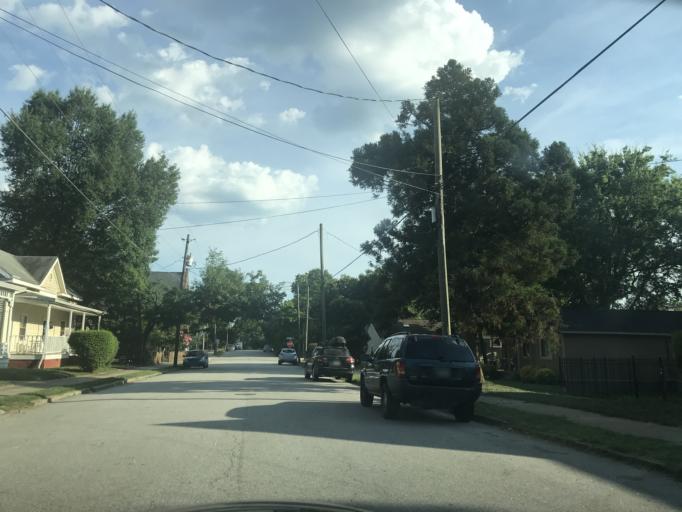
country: US
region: North Carolina
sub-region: Wake County
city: Raleigh
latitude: 35.7773
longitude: -78.6292
